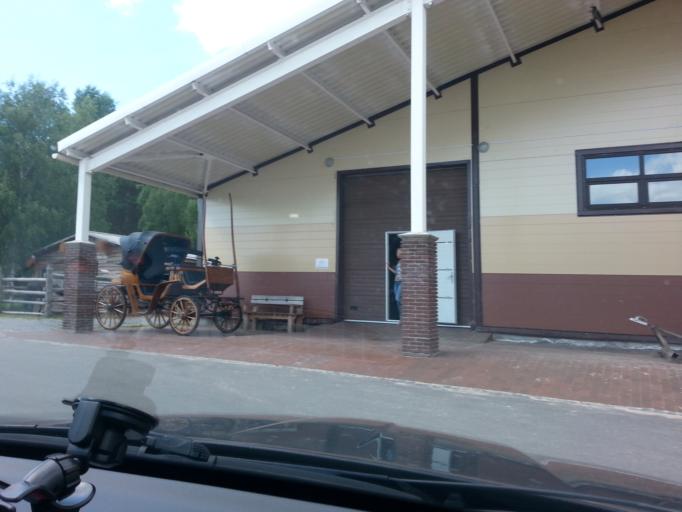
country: BY
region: Minsk
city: Narach
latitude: 54.8620
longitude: 26.7114
